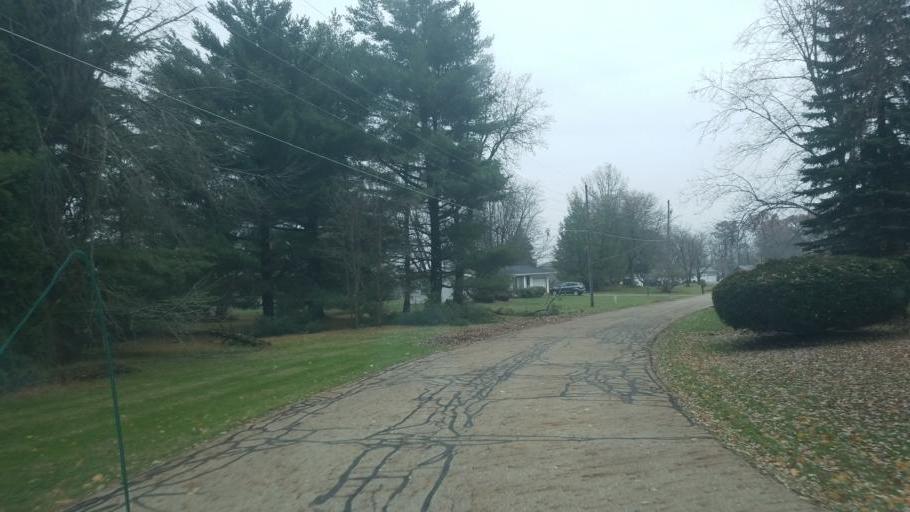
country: US
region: Ohio
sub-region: Richland County
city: Lexington
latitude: 40.7046
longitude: -82.5349
